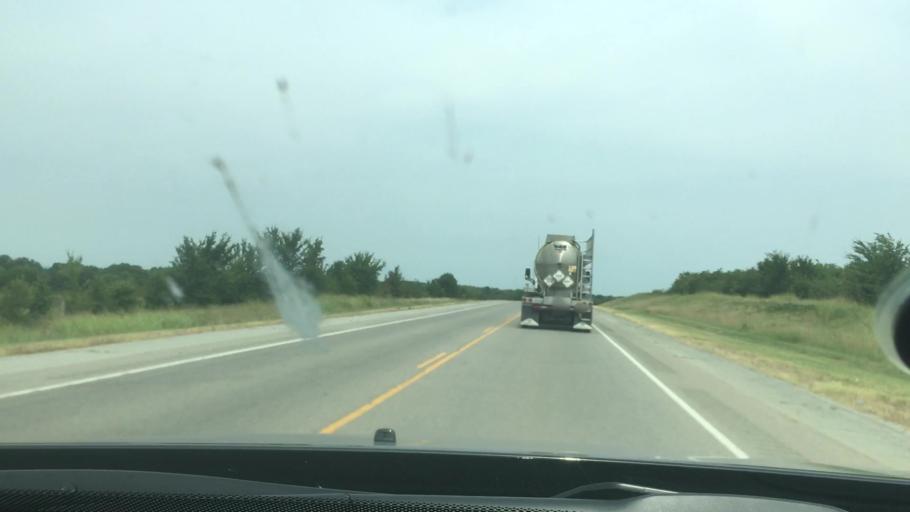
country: US
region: Oklahoma
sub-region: Pontotoc County
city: Ada
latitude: 34.6365
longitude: -96.4789
